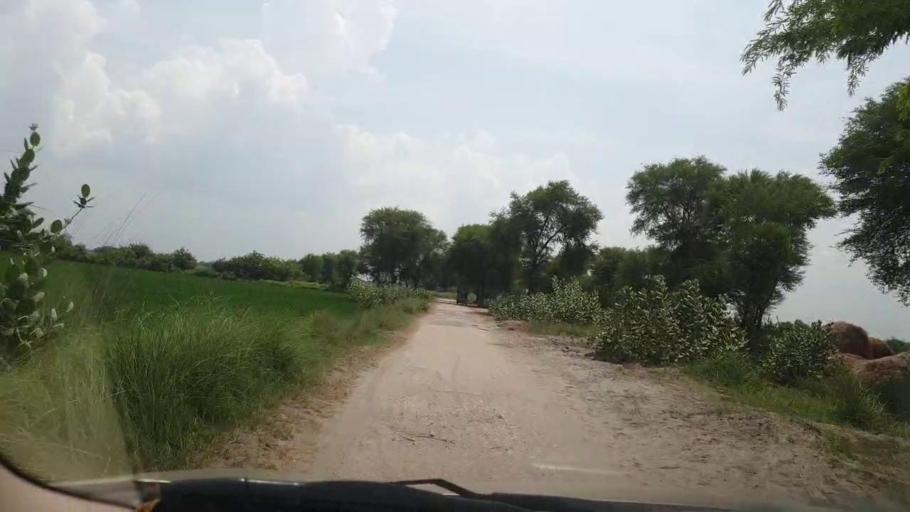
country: PK
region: Sindh
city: Larkana
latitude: 27.5970
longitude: 68.1236
